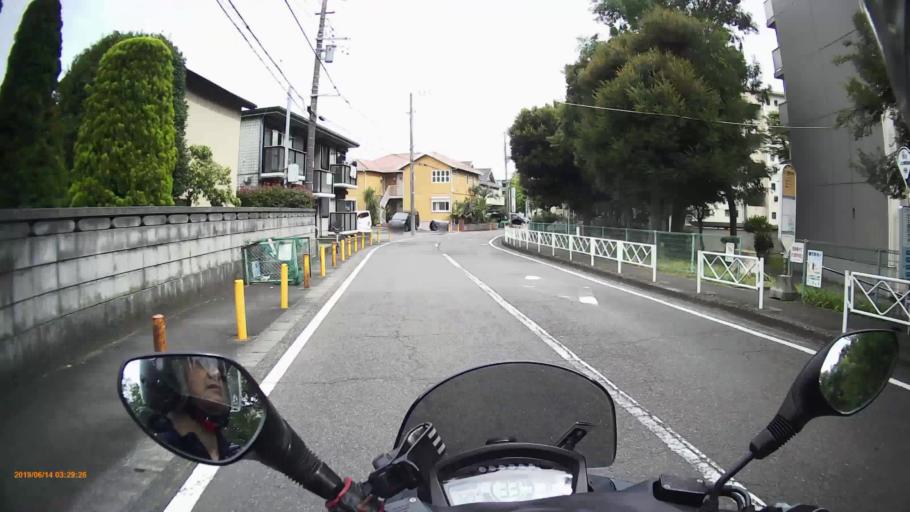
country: JP
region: Kanagawa
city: Minami-rinkan
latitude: 35.4147
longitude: 139.4492
